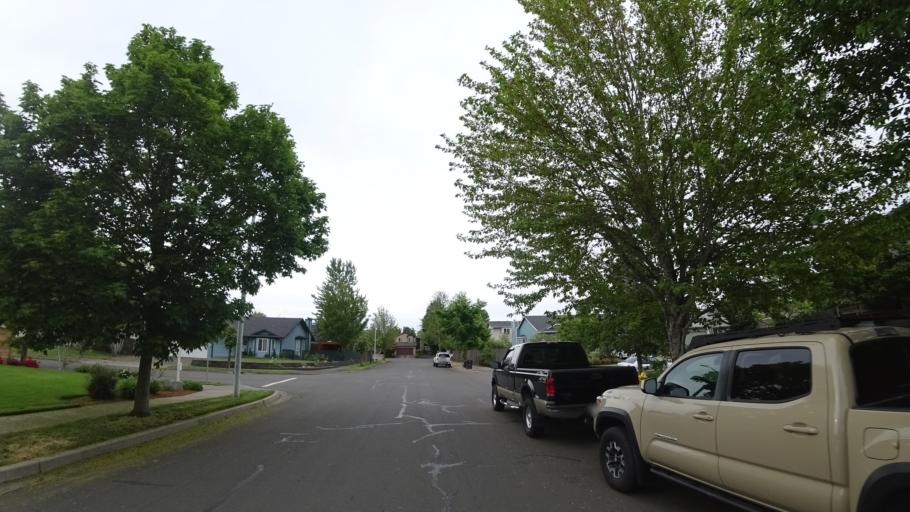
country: US
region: Oregon
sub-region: Washington County
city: Aloha
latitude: 45.5133
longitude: -122.9079
